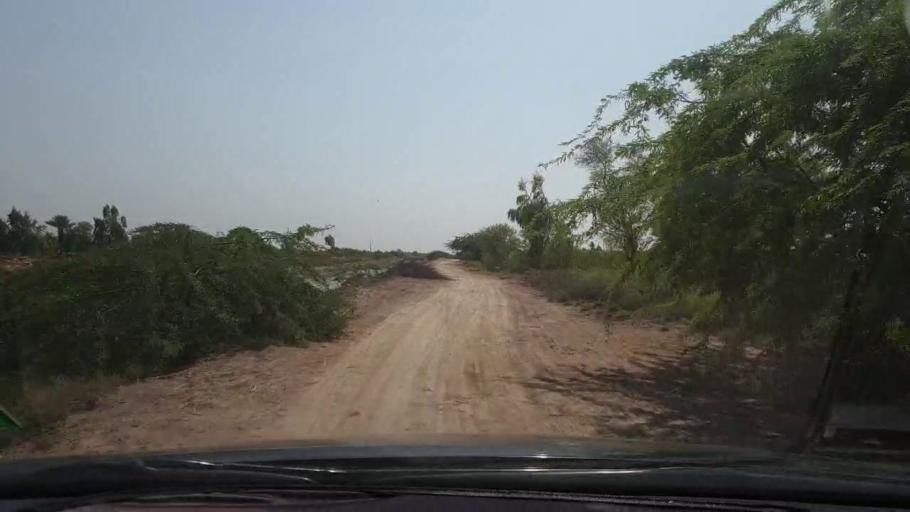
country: PK
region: Sindh
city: Tando Bago
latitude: 24.7934
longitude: 69.1114
